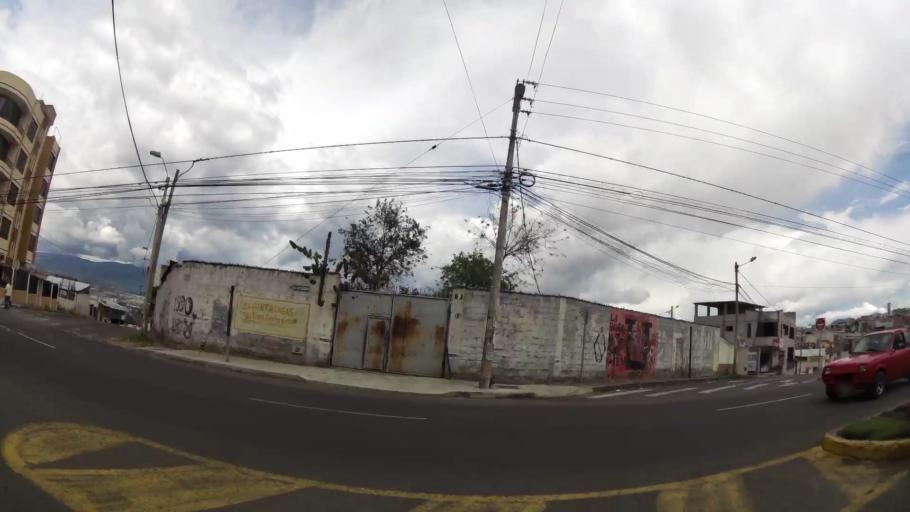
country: EC
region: Tungurahua
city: Ambato
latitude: -1.2489
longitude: -78.6219
